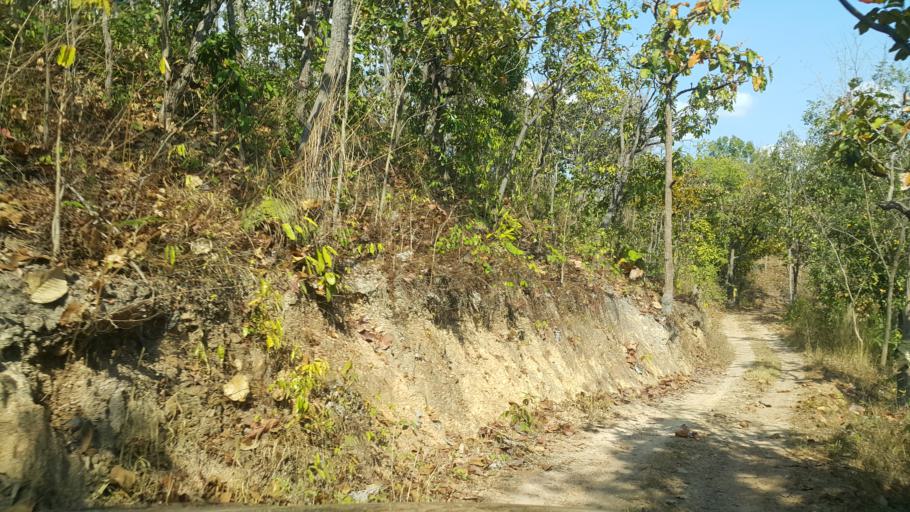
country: TH
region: Sukhothai
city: Thung Saliam
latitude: 17.3424
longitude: 99.5883
